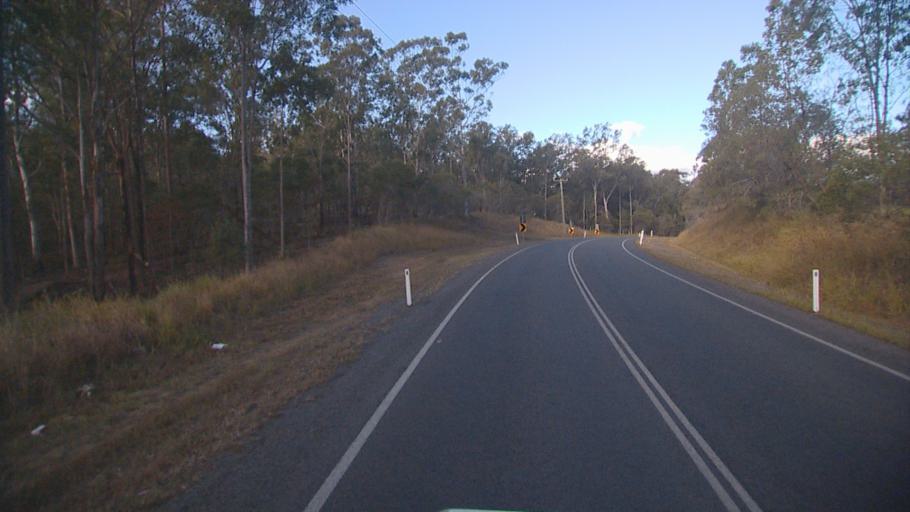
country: AU
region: Queensland
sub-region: Logan
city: Cedar Vale
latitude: -27.8671
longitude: 153.0624
